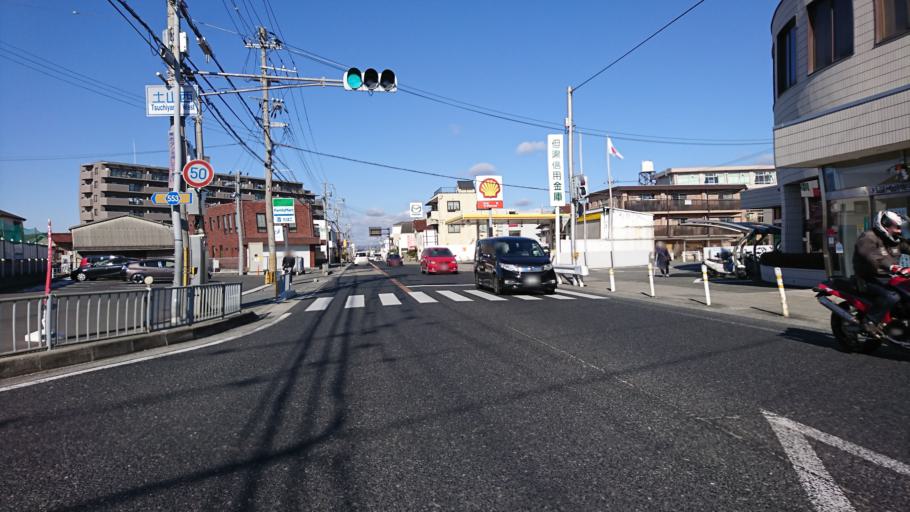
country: JP
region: Hyogo
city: Kakogawacho-honmachi
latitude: 34.7229
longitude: 134.8897
